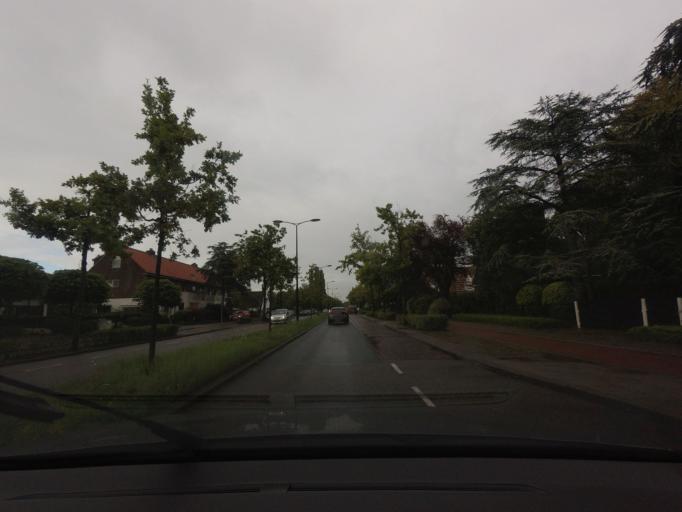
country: NL
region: South Holland
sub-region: Gemeente Voorschoten
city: Voorschoten
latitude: 52.1154
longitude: 4.4345
